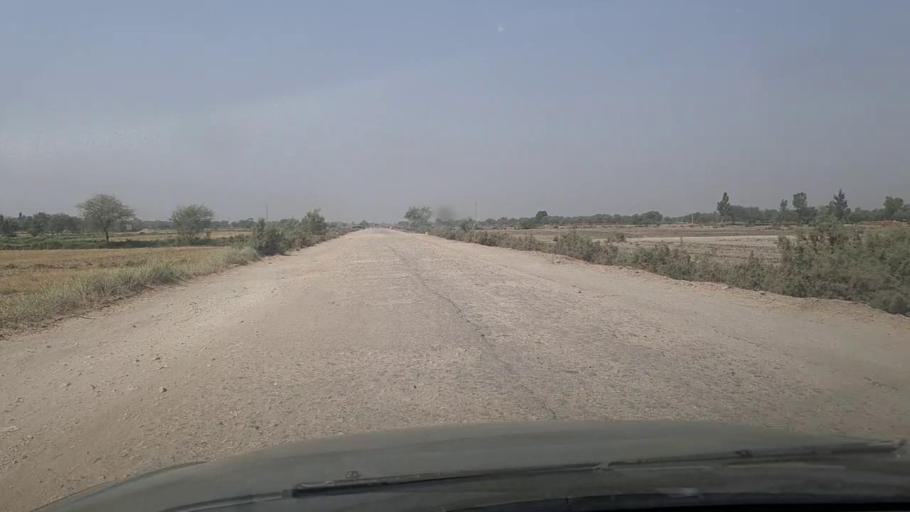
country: PK
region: Sindh
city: Khanpur
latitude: 27.9091
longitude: 69.5104
